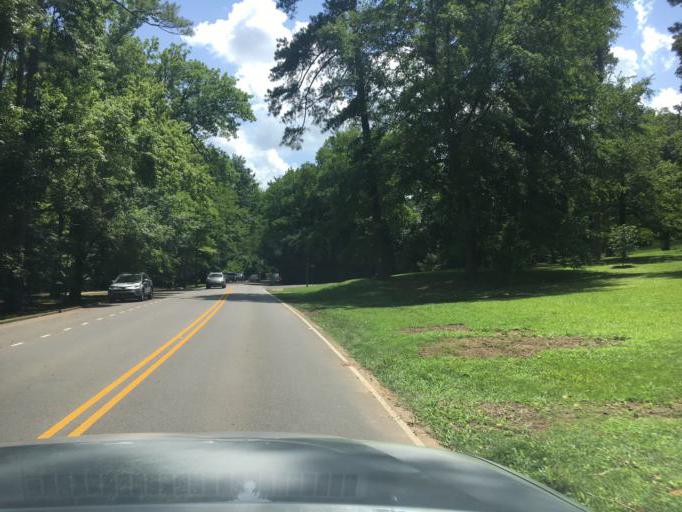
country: US
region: Alabama
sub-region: Jefferson County
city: Mountain Brook
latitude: 33.4775
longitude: -86.7625
